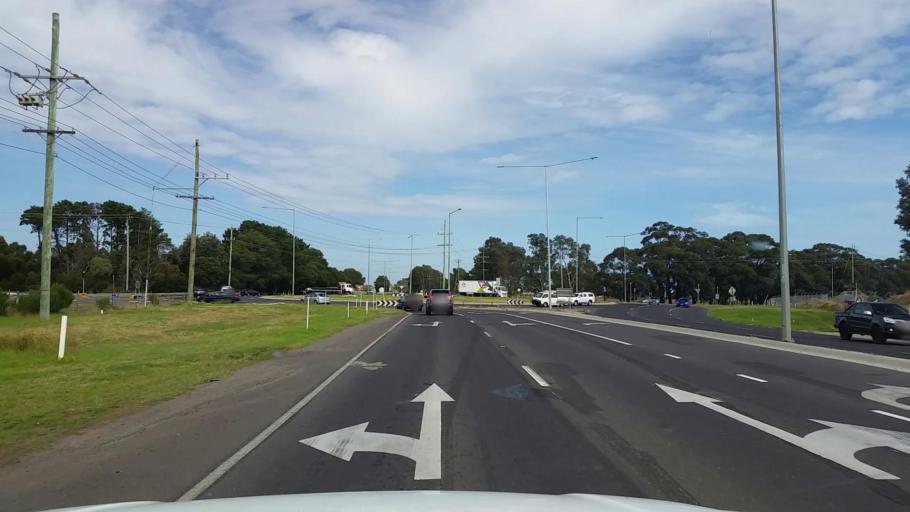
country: AU
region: Victoria
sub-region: Frankston
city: Sandhurst
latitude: -38.0710
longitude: 145.1958
